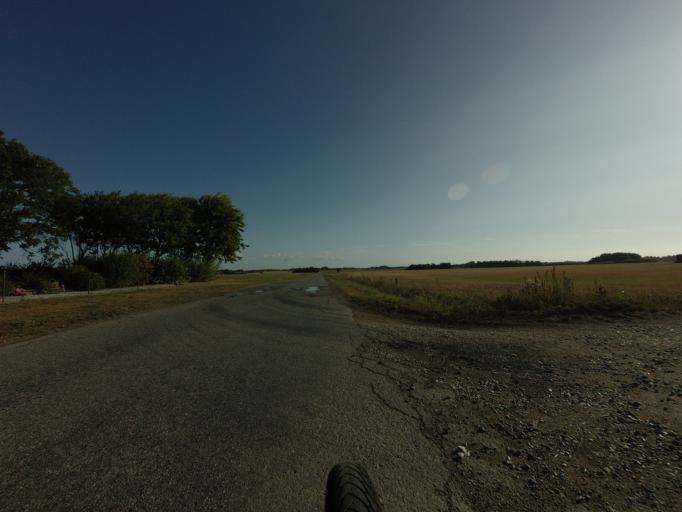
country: DK
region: North Denmark
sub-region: Hjorring Kommune
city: Vra
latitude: 57.3824
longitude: 9.9222
